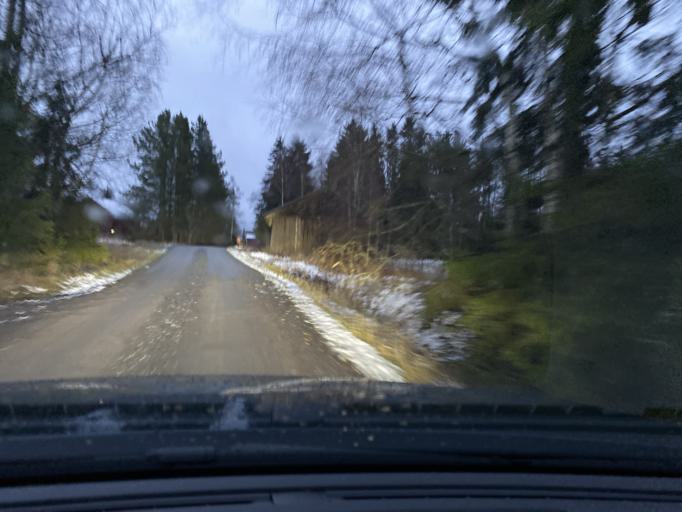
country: FI
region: Pirkanmaa
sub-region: Lounais-Pirkanmaa
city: Punkalaidun
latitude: 61.1178
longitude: 23.0259
